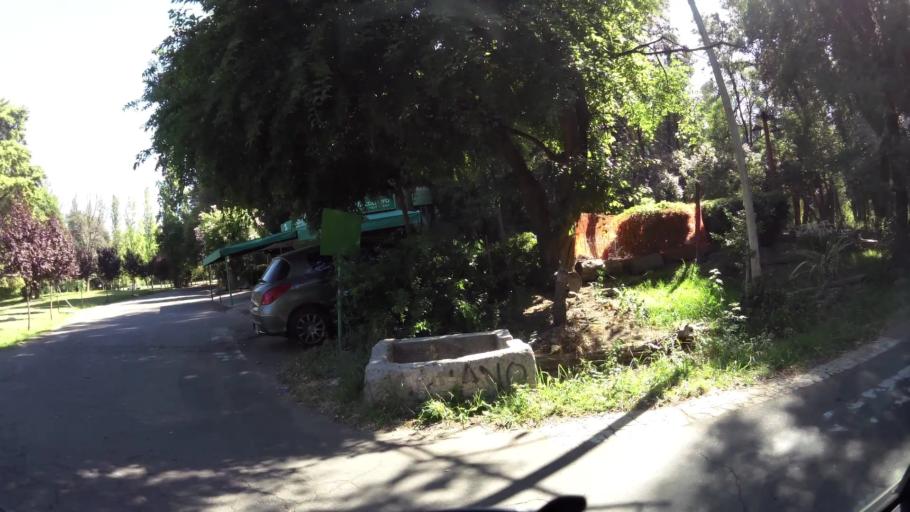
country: AR
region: Mendoza
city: Mendoza
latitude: -32.8860
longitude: -68.8698
